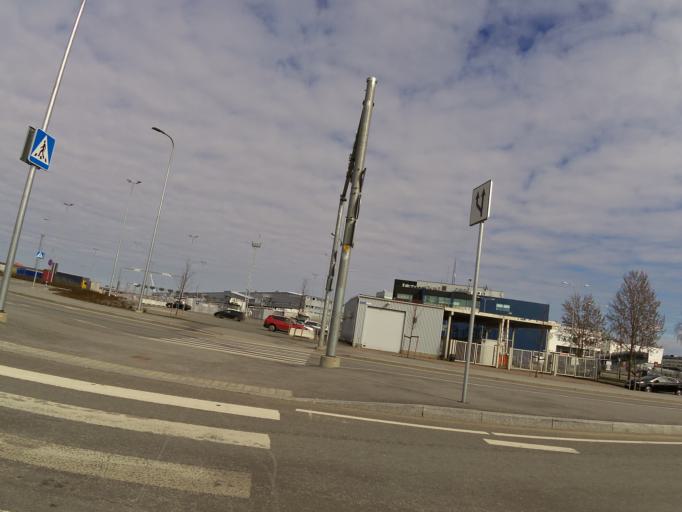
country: EE
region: Harju
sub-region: Tallinna linn
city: Tallinn
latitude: 59.4450
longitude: 24.7581
